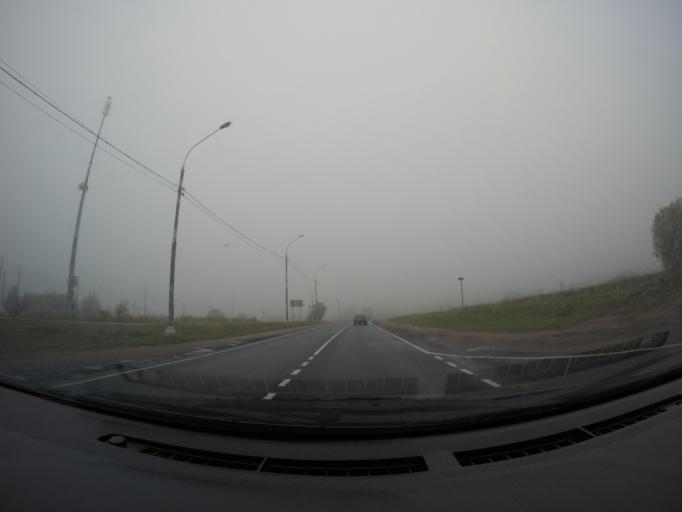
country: RU
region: Moskovskaya
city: Ruza
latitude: 55.7697
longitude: 36.2640
